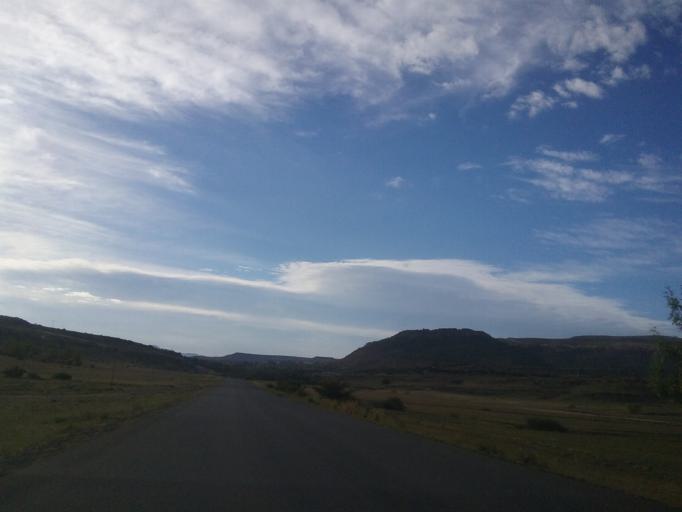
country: LS
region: Quthing
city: Quthing
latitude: -30.3861
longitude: 27.6003
